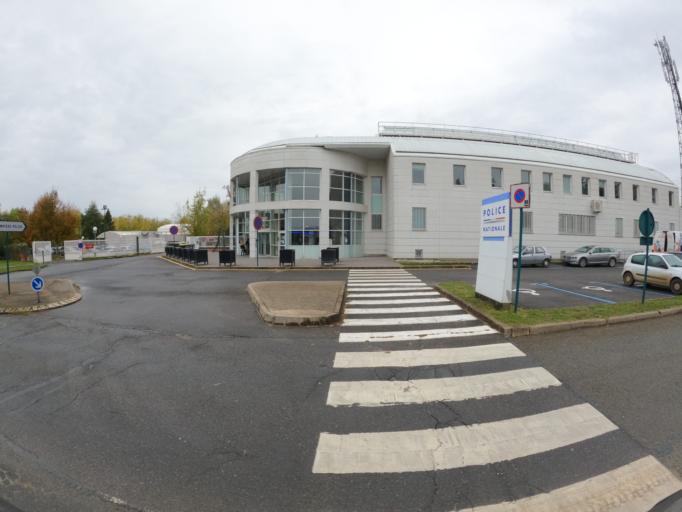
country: FR
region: Ile-de-France
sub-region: Departement de Seine-et-Marne
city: Serris
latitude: 48.8611
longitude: 2.7862
